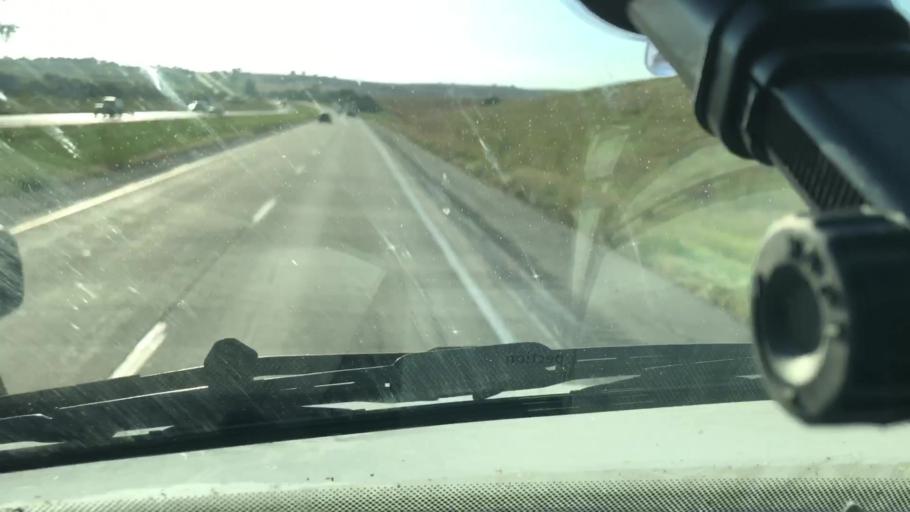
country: US
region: Iowa
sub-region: Pottawattamie County
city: Avoca
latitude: 41.5003
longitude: -95.5155
